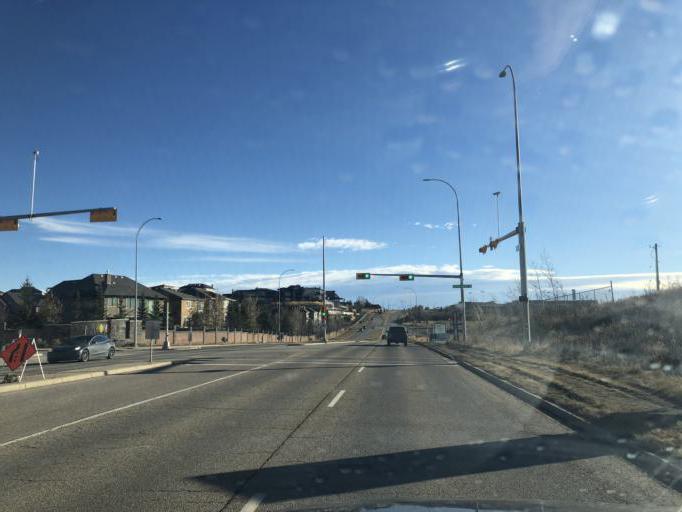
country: CA
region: Alberta
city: Calgary
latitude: 51.0378
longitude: -114.2044
